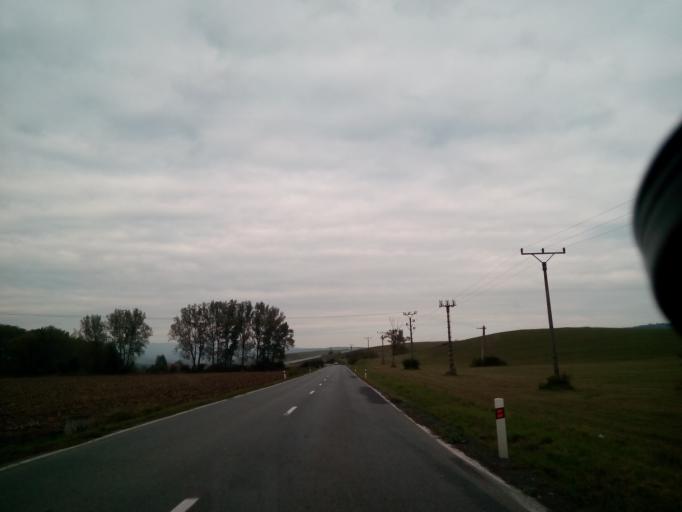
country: SK
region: Presovsky
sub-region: Okres Presov
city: Presov
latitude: 49.0623
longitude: 21.3433
